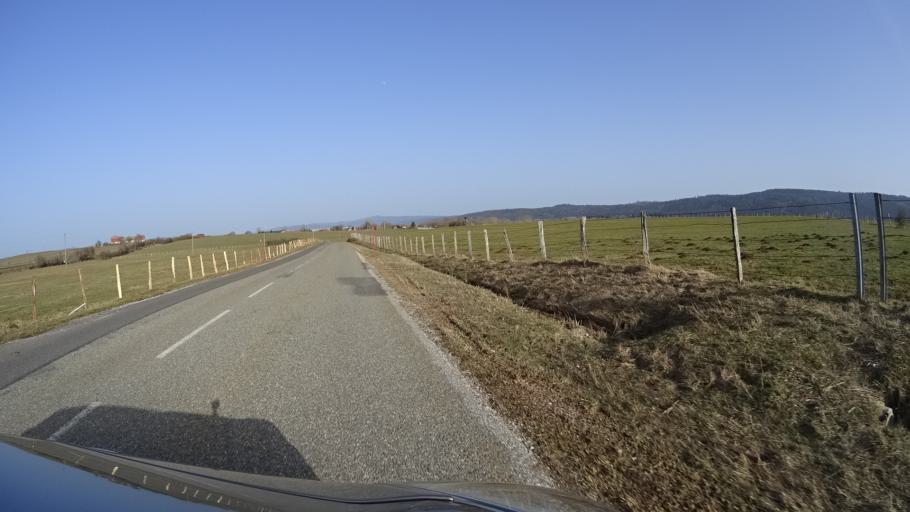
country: FR
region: Franche-Comte
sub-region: Departement du Doubs
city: Frasne
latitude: 46.8660
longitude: 6.2023
